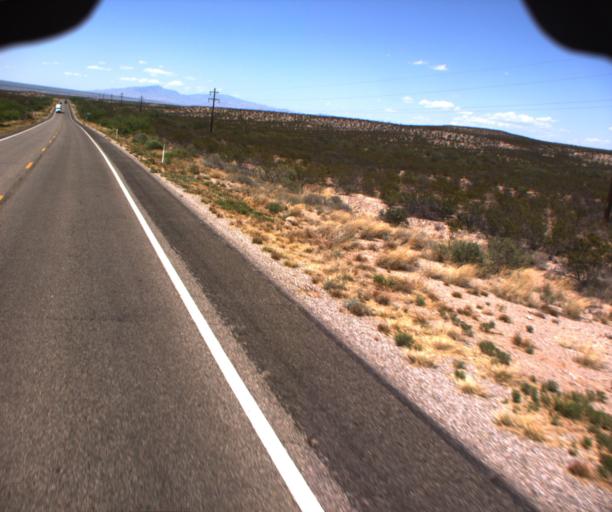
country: US
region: Arizona
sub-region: Cochise County
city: Tombstone
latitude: 31.7762
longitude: -110.1317
